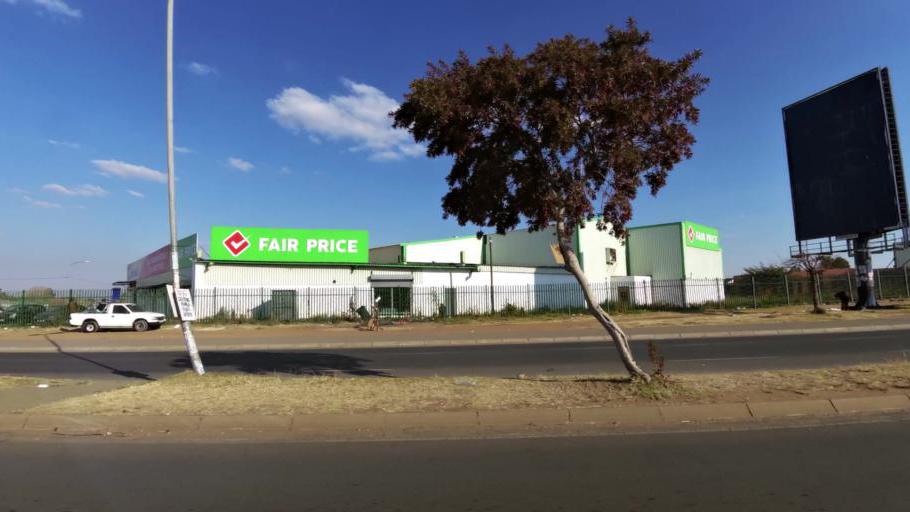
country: ZA
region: Gauteng
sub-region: City of Johannesburg Metropolitan Municipality
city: Roodepoort
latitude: -26.2144
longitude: 27.8751
